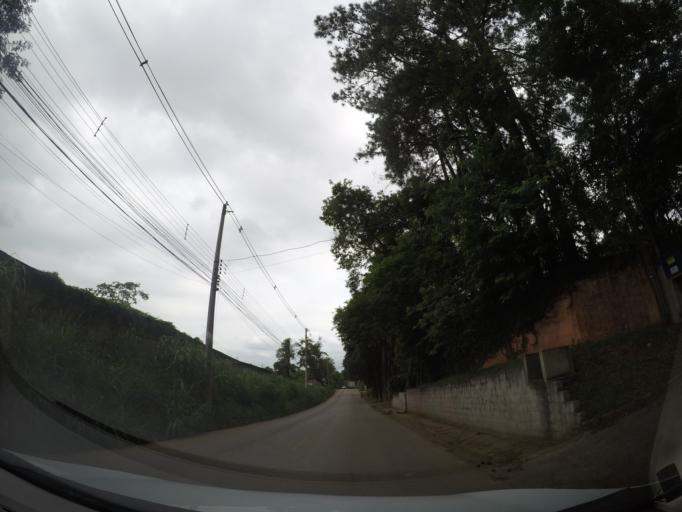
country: BR
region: Sao Paulo
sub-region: Aruja
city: Aruja
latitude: -23.3892
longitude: -46.3966
